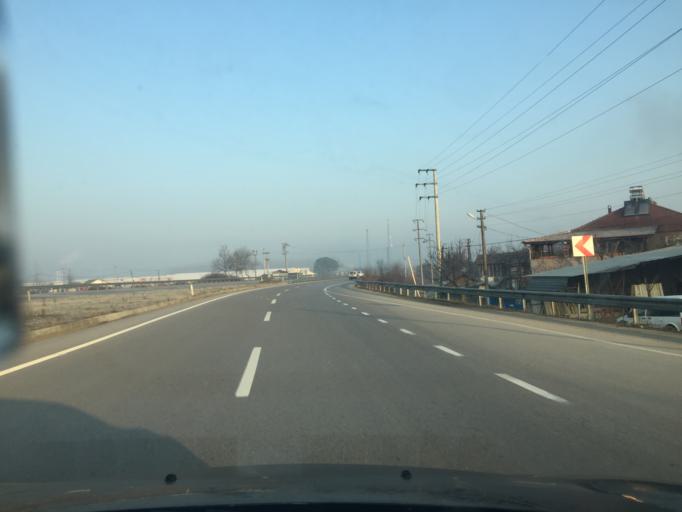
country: TR
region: Sakarya
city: Akyazi
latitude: 40.7125
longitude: 30.5644
